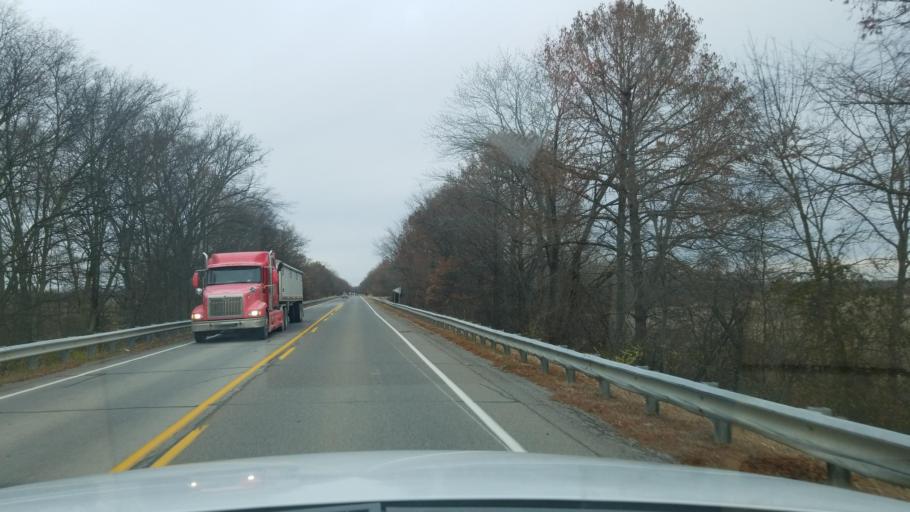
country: US
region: Indiana
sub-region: Posey County
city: Mount Vernon
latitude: 37.9315
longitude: -88.0031
